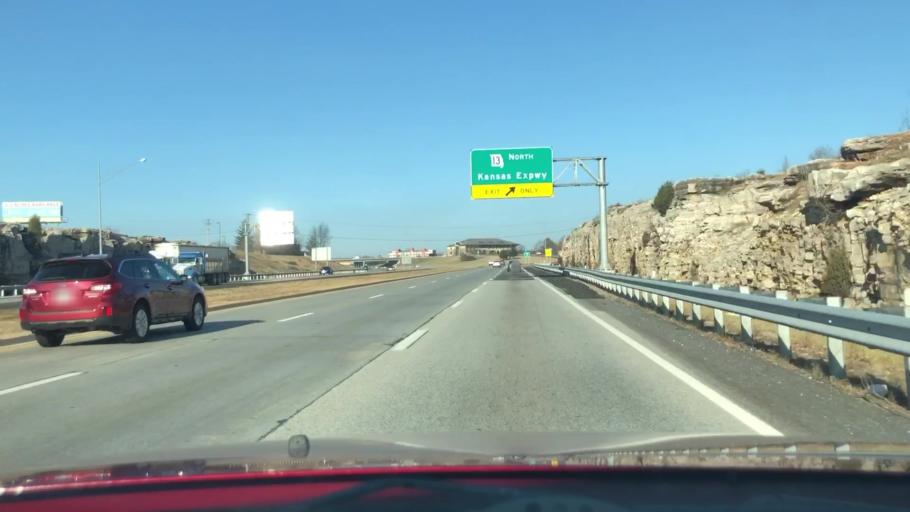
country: US
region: Missouri
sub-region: Greene County
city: Battlefield
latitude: 37.1395
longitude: -93.3124
